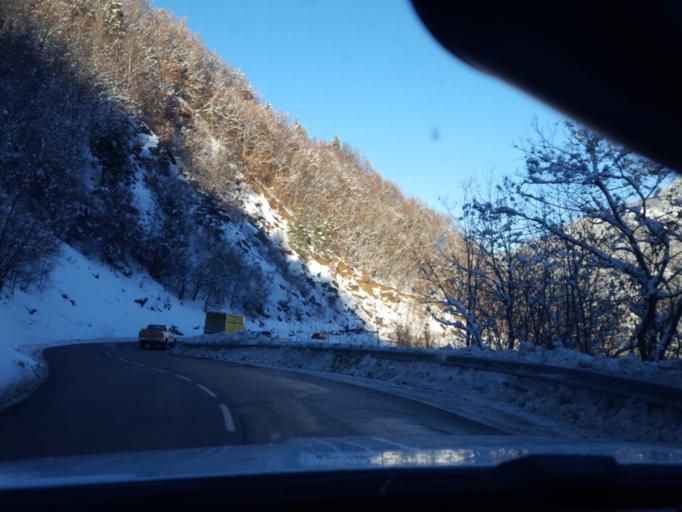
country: FR
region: Rhone-Alpes
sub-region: Departement de la Savoie
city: Salins-les-Thermes
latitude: 45.4608
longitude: 6.5148
